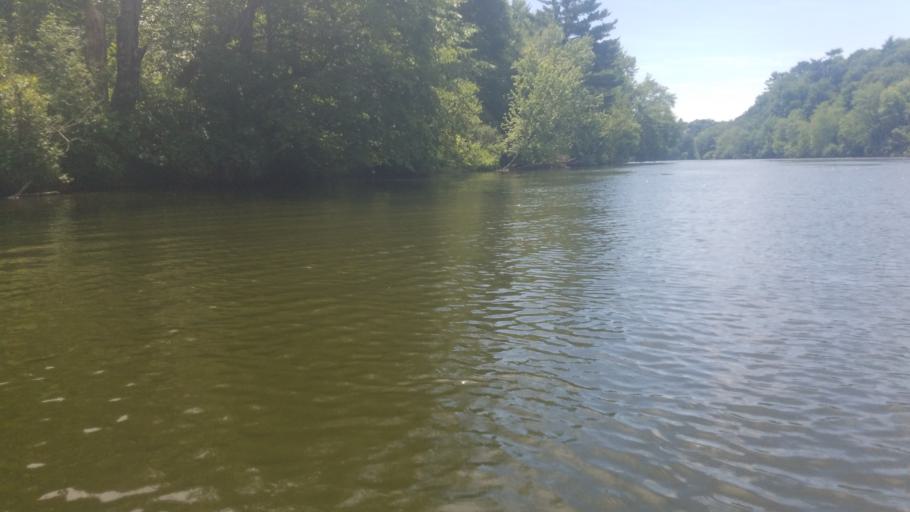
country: US
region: Wisconsin
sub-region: Dunn County
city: Menomonie
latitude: 44.8700
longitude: -91.9422
